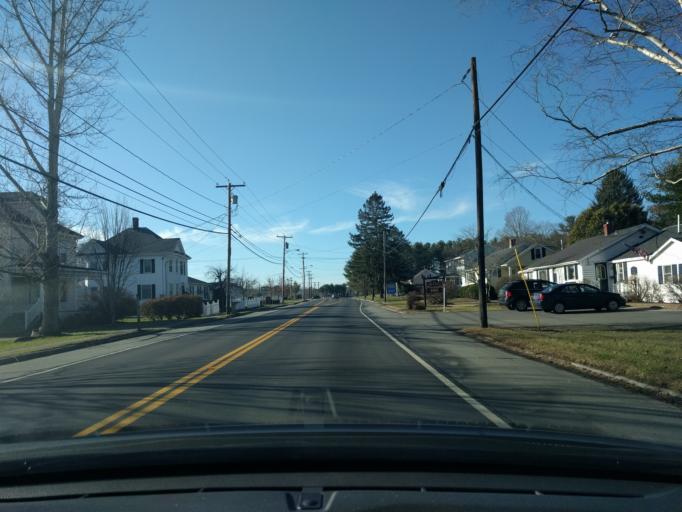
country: US
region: Maine
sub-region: Penobscot County
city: Hampden
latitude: 44.7449
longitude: -68.8412
